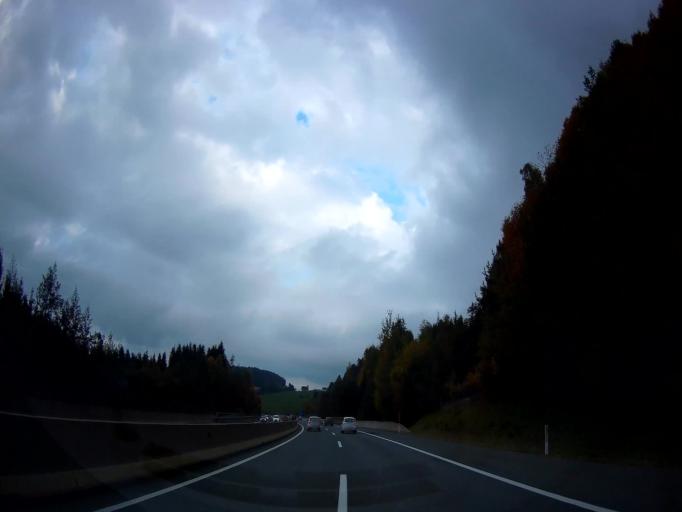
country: AT
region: Styria
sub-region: Politischer Bezirk Voitsberg
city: Ligist
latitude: 46.9709
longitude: 15.1995
